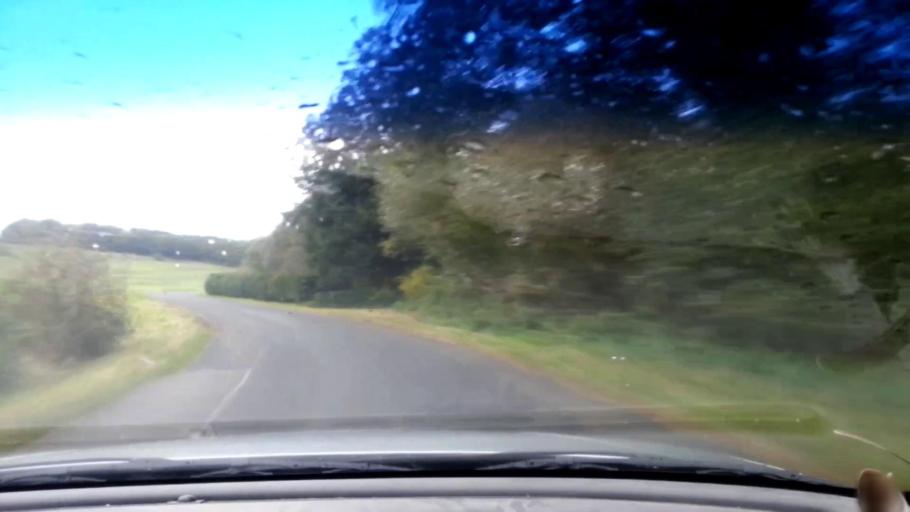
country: DE
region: Bavaria
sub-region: Upper Franconia
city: Priesendorf
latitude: 49.8652
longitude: 10.6633
